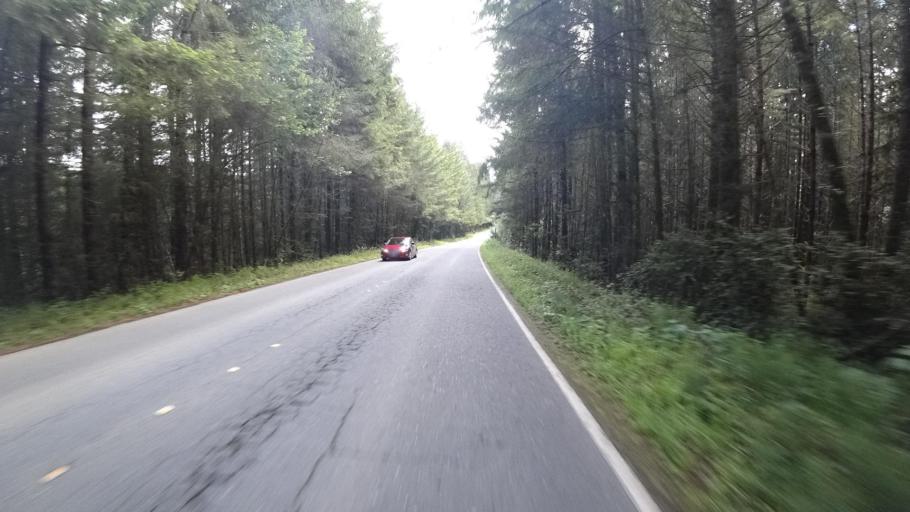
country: US
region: California
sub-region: Humboldt County
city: McKinleyville
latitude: 40.9704
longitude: -124.0512
